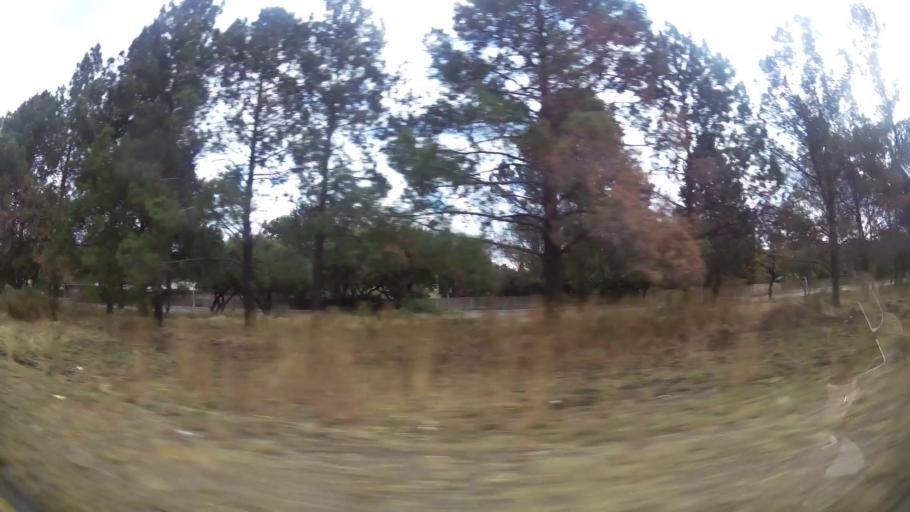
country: ZA
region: Orange Free State
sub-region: Fezile Dabi District Municipality
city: Sasolburg
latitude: -26.8062
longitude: 27.8359
